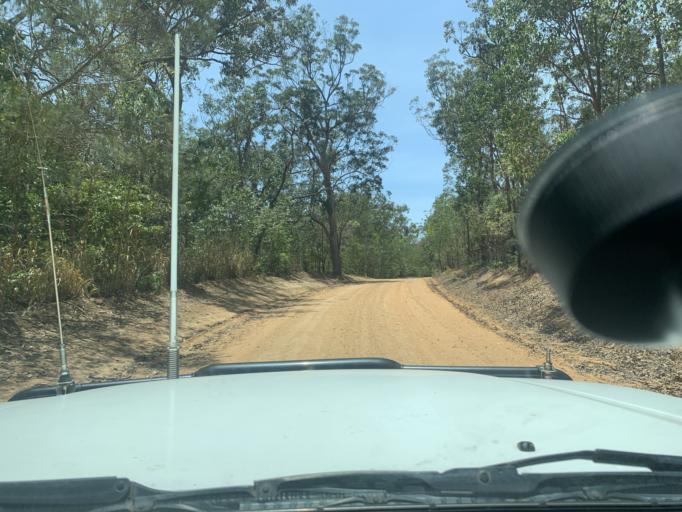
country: AU
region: Queensland
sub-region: Tablelands
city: Kuranda
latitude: -16.9186
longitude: 145.5922
